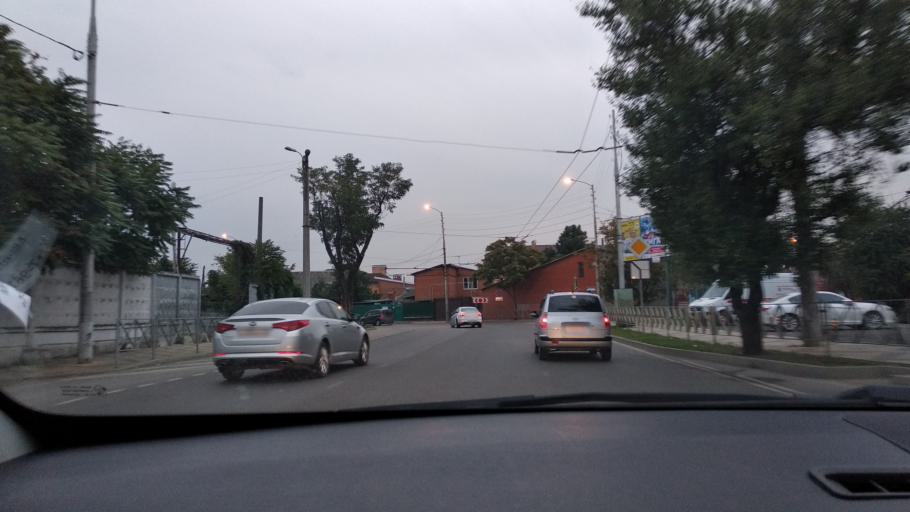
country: RU
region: Adygeya
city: Yablonovskiy
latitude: 45.0134
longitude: 38.9582
